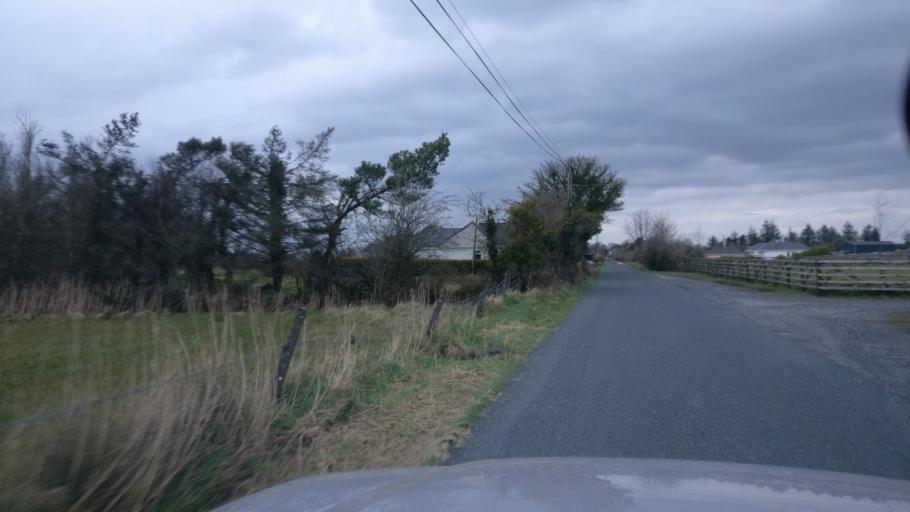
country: IE
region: Connaught
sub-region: County Galway
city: Loughrea
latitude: 53.2430
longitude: -8.5182
